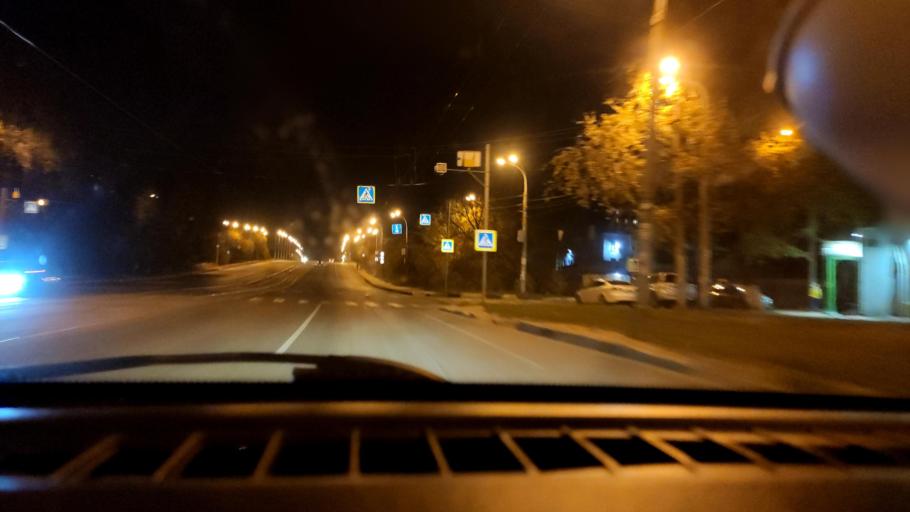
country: RU
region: Samara
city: Samara
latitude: 53.2165
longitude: 50.2664
